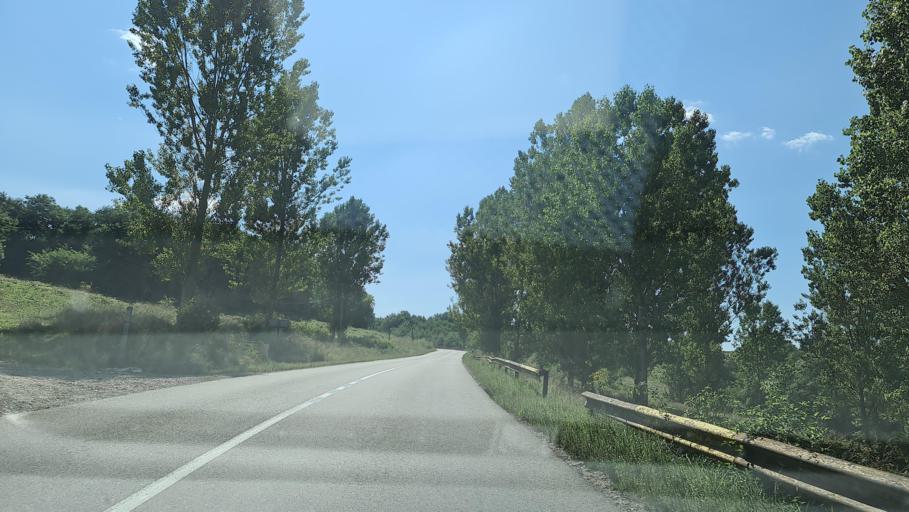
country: RO
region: Bacau
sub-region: Comuna Scorteni
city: Scorteni
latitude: 46.5612
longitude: 26.6231
